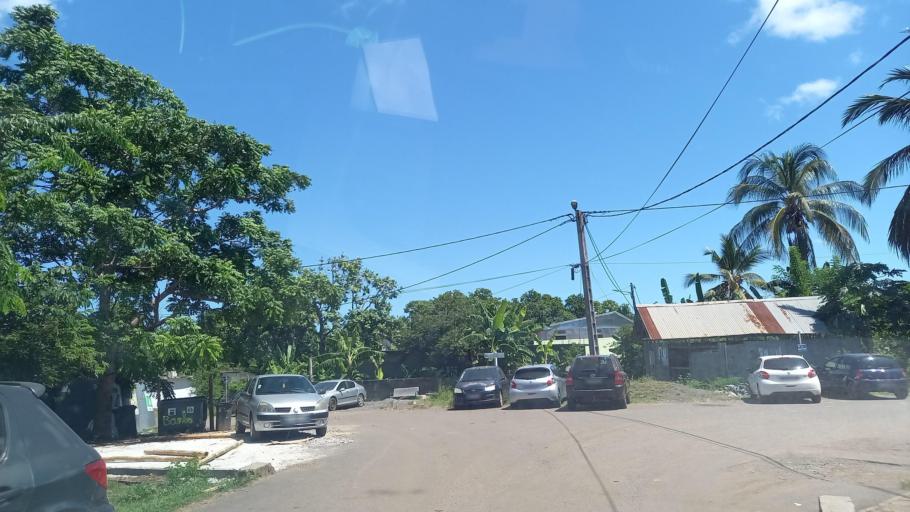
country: YT
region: Boueni
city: Boueni
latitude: -12.9243
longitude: 45.0900
